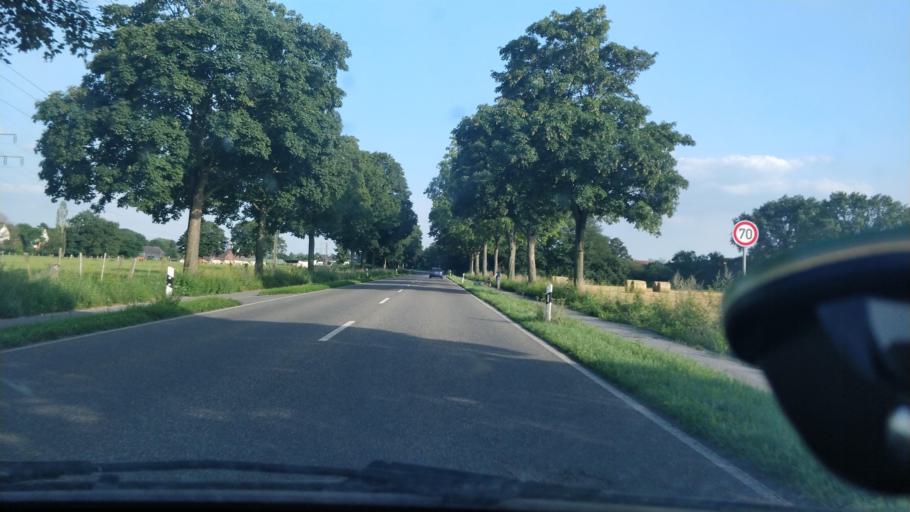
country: DE
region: North Rhine-Westphalia
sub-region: Regierungsbezirk Dusseldorf
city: Kamp-Lintfort
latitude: 51.5192
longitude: 6.5334
